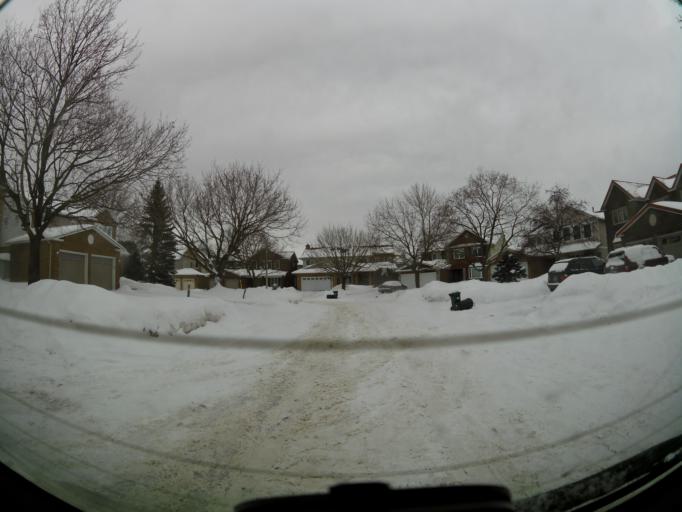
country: CA
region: Ontario
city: Ottawa
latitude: 45.3720
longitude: -75.6176
